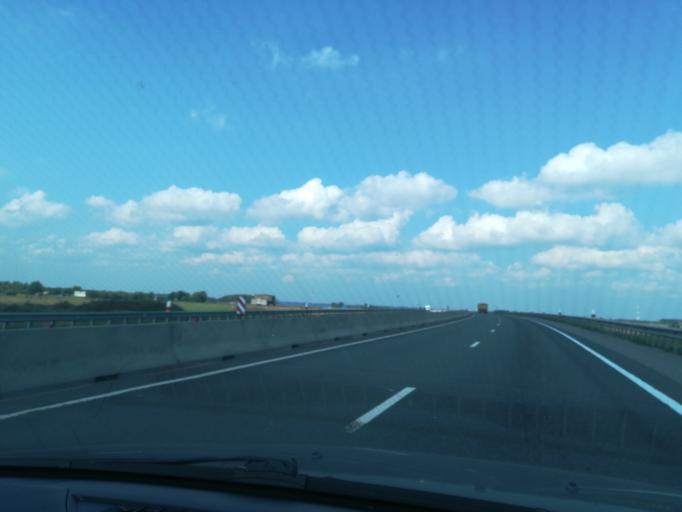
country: RU
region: Leningrad
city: Sista-Palkino
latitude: 59.5835
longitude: 28.7683
